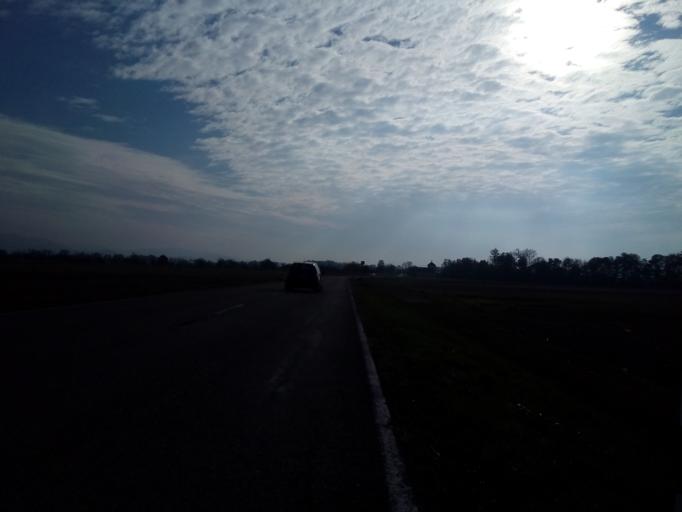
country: DE
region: Baden-Wuerttemberg
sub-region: Karlsruhe Region
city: Zell
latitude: 48.7028
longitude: 8.0682
